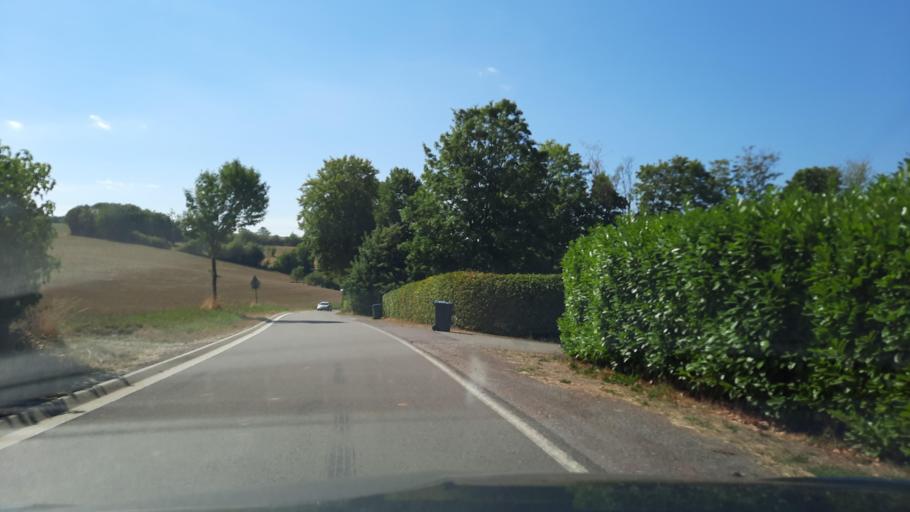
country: DE
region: Rheinland-Pfalz
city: Zerf
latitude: 49.6047
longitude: 6.6525
